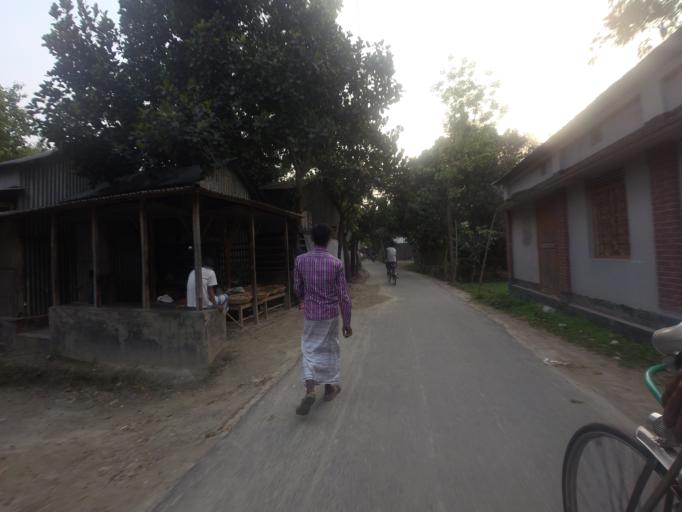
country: BD
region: Rajshahi
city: Sirajganj
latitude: 24.3312
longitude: 89.6809
